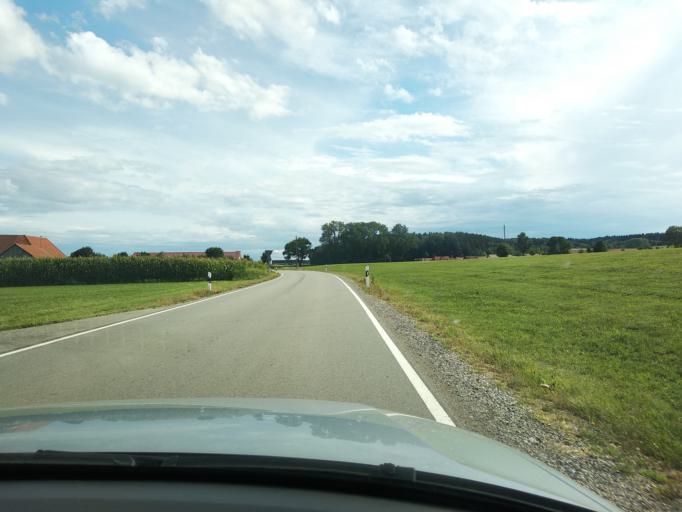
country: DE
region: Bavaria
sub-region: Swabia
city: Wolfertschwenden
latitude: 47.8792
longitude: 10.2350
